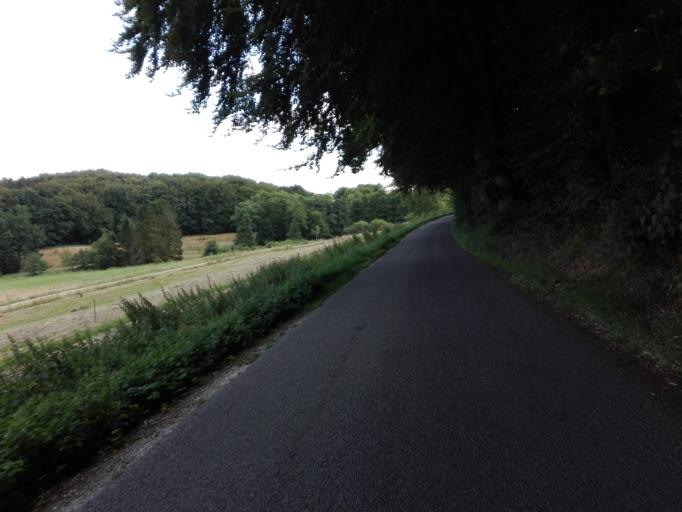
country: DK
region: Central Jutland
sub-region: Skanderborg Kommune
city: Horning
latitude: 56.1044
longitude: 10.0162
